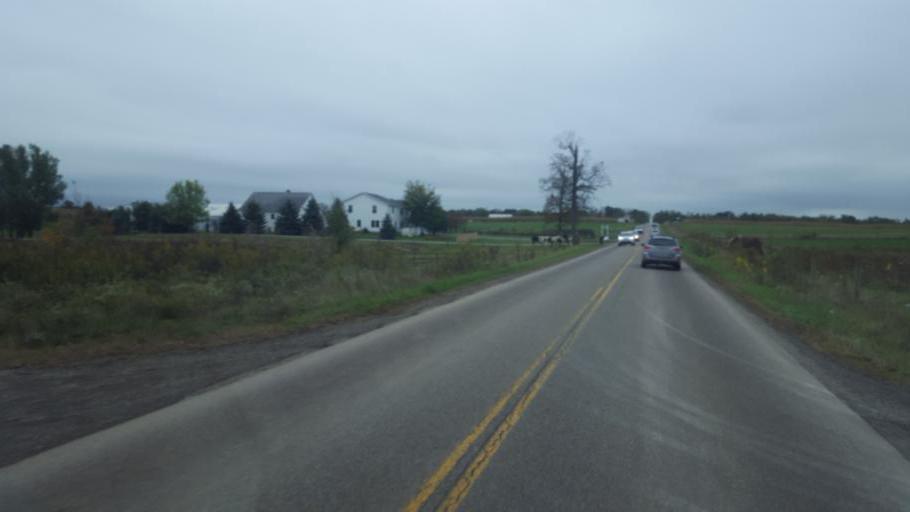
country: US
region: Ohio
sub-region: Wayne County
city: Apple Creek
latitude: 40.6781
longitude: -81.7840
